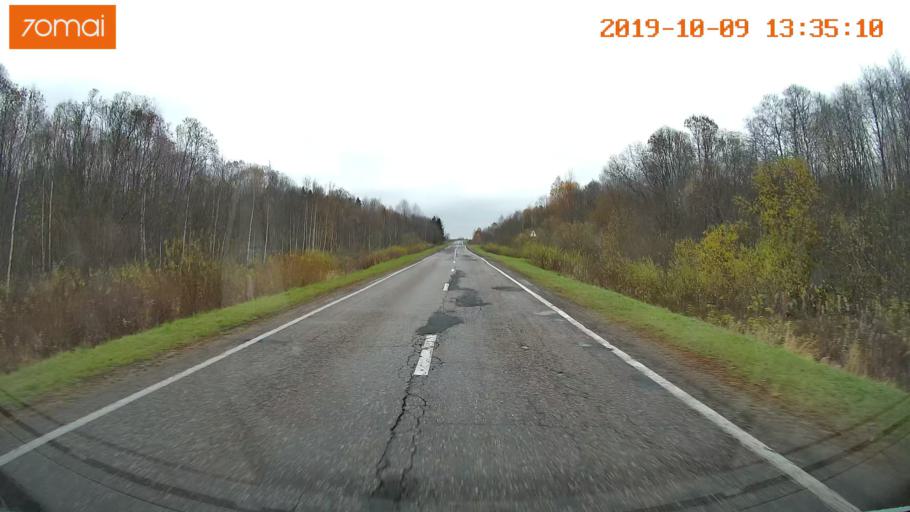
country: RU
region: Jaroslavl
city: Lyubim
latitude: 58.3345
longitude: 41.0731
